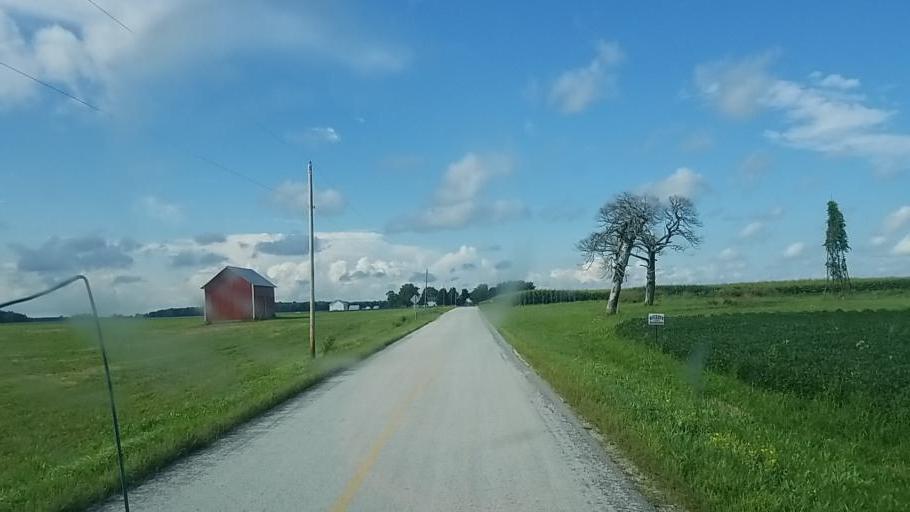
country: US
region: Ohio
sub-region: Hardin County
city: Forest
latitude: 40.7314
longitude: -83.5159
